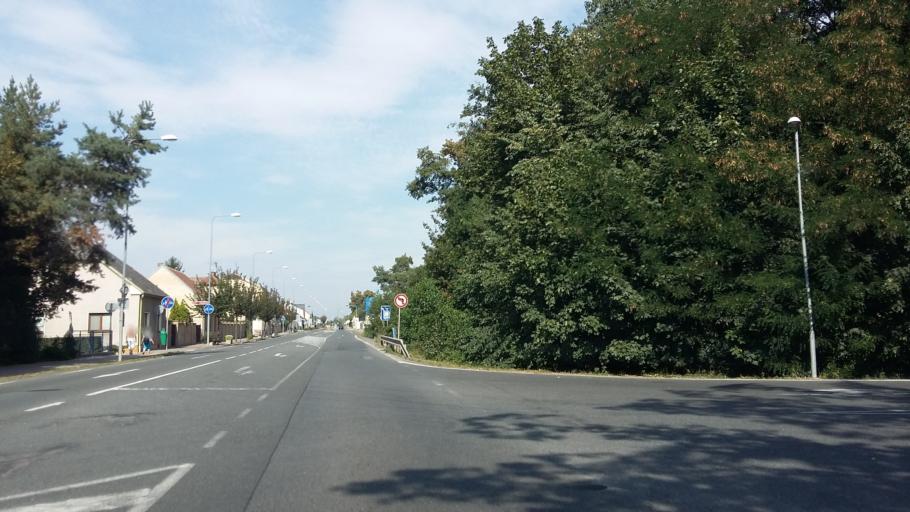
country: CZ
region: Central Bohemia
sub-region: Okres Kolin
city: Kolin
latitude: 50.0457
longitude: 15.2174
